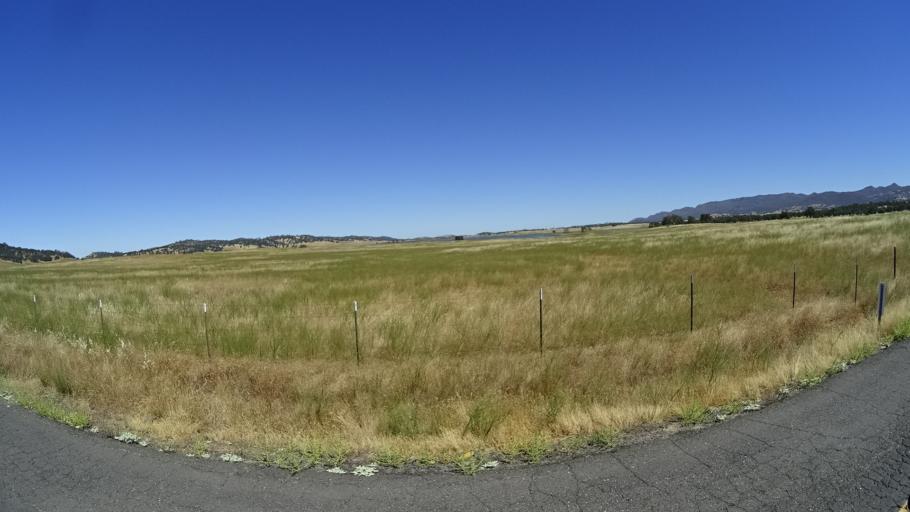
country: US
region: California
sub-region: Calaveras County
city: Copperopolis
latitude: 38.0228
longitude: -120.7407
